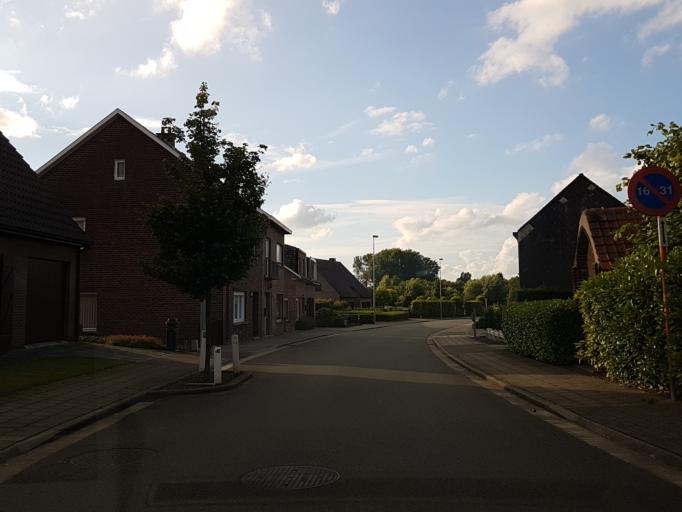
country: BE
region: Flanders
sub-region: Provincie Vlaams-Brabant
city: Opwijk
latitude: 50.9535
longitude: 4.1363
